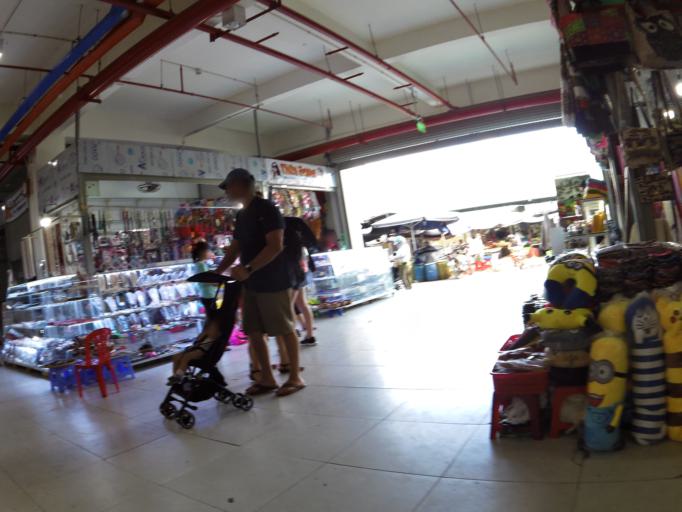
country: VN
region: Khanh Hoa
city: Nha Trang
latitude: 12.2553
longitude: 109.1915
